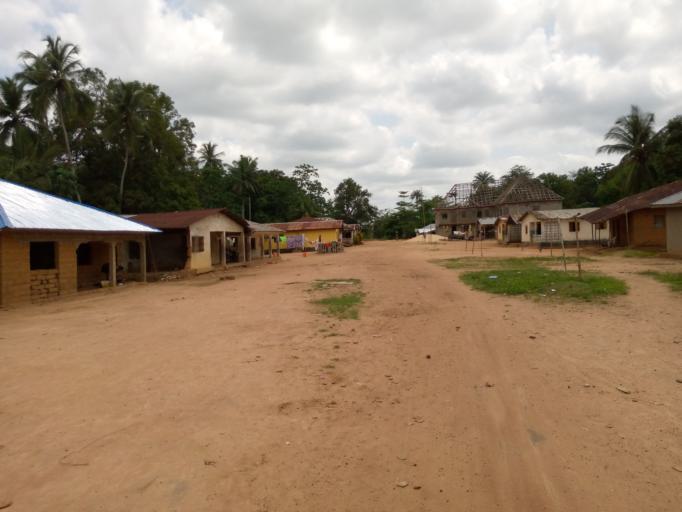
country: SL
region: Western Area
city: Waterloo
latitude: 8.4037
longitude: -12.9494
